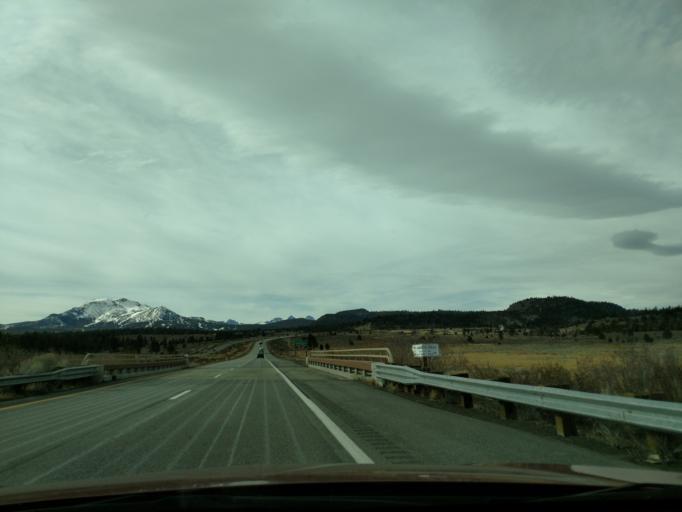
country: US
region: California
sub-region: Mono County
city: Mammoth Lakes
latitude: 37.6380
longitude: -118.9028
